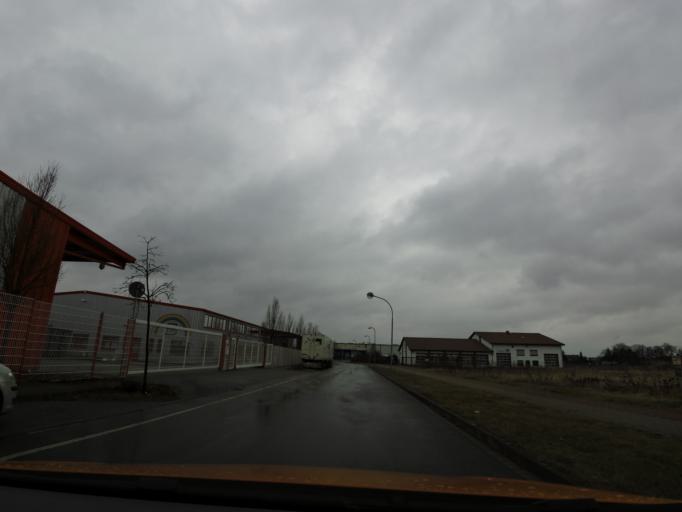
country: DE
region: Brandenburg
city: Rangsdorf
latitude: 52.3127
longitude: 13.4405
